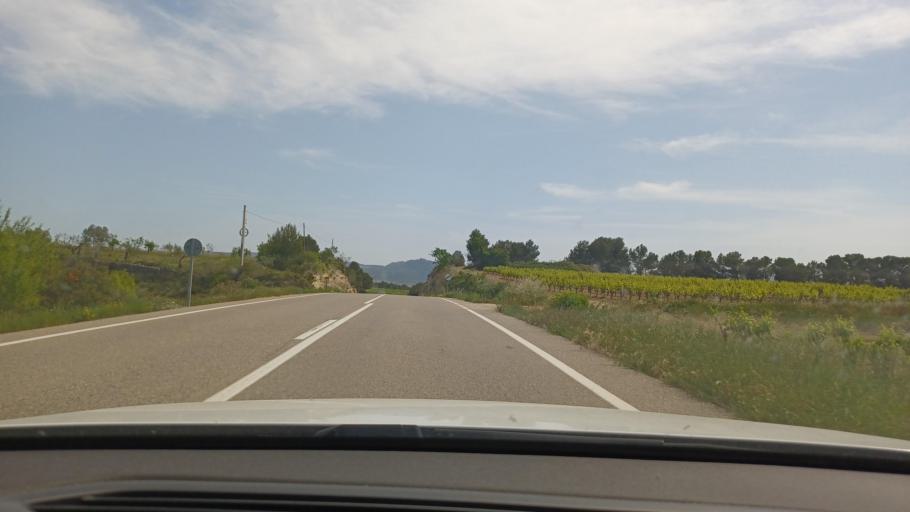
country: ES
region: Catalonia
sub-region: Provincia de Tarragona
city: Vilalba dels Arcs
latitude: 41.0942
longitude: 0.4185
